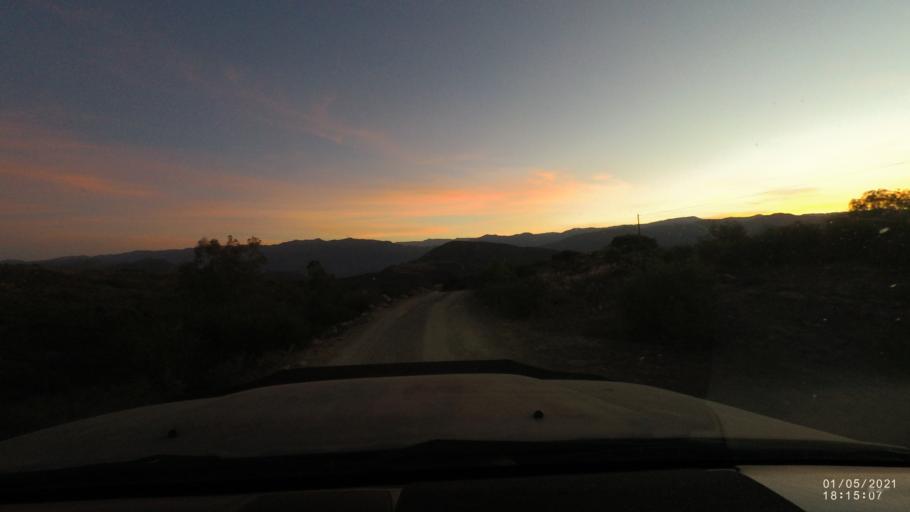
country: BO
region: Cochabamba
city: Capinota
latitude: -17.6734
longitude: -66.2143
